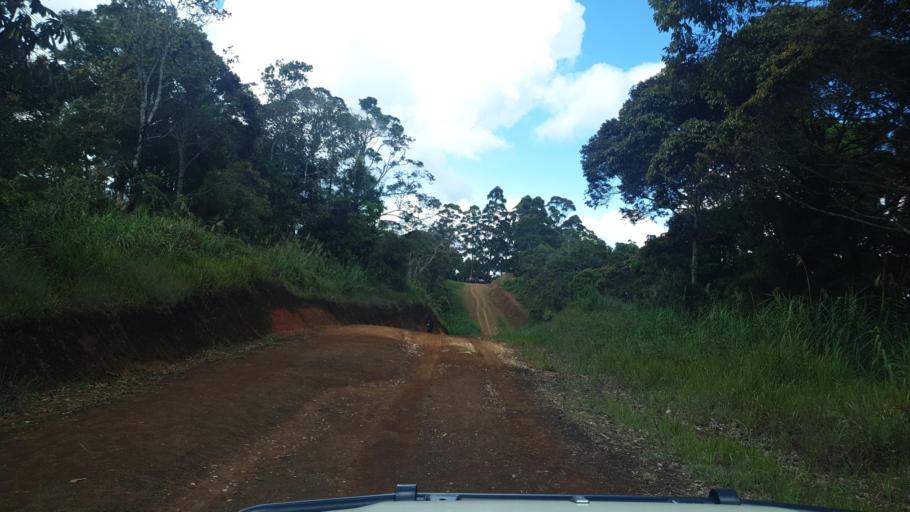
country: PG
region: Eastern Highlands
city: Goroka
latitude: -6.2790
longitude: 145.1967
